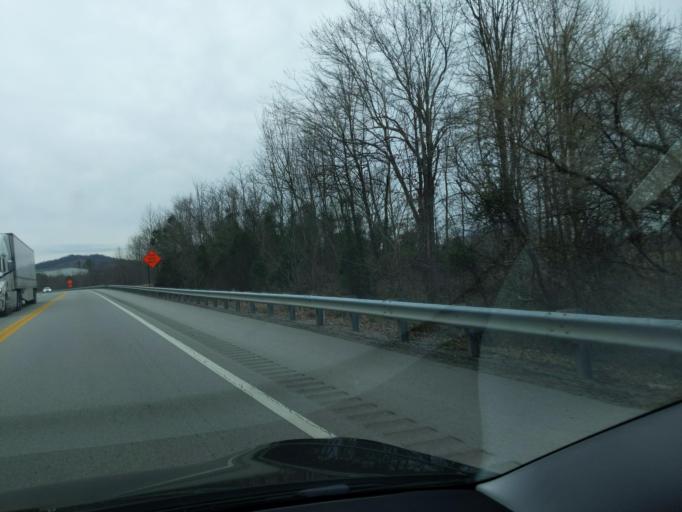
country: US
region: Kentucky
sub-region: Whitley County
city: Corbin
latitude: 36.9137
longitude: -84.0674
